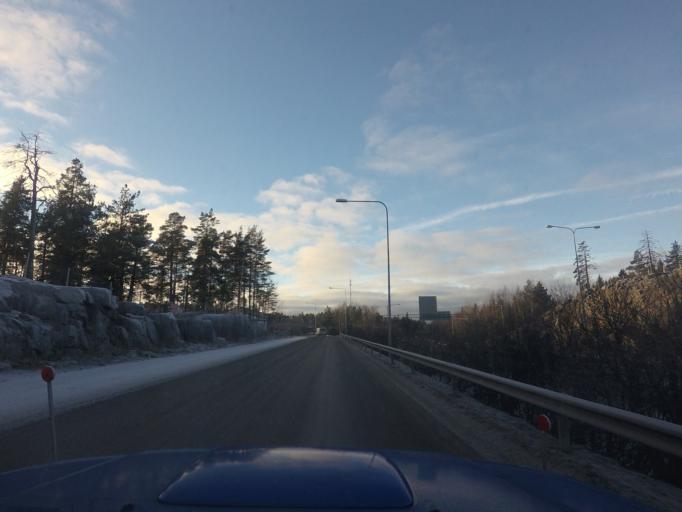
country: FI
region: Uusimaa
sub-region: Helsinki
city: Espoo
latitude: 60.2064
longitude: 24.6261
